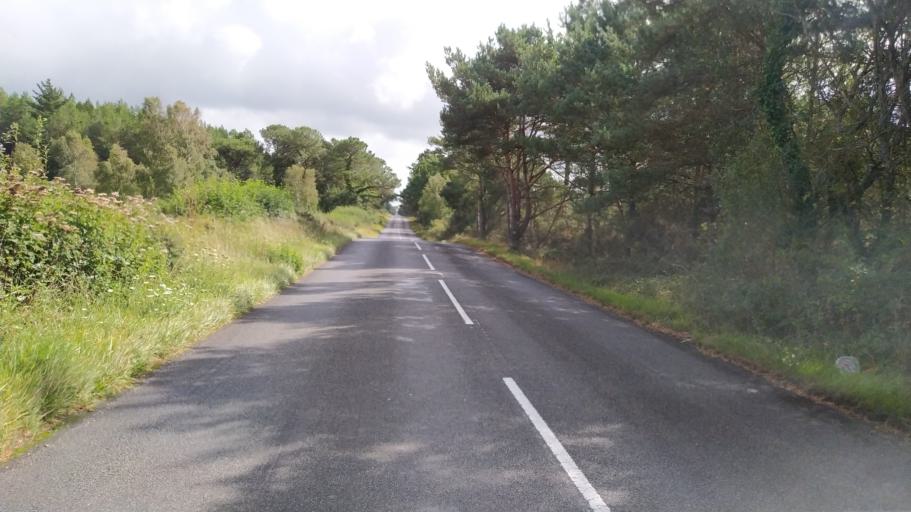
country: GB
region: England
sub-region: Dorset
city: Wareham
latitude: 50.7238
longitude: -2.1161
